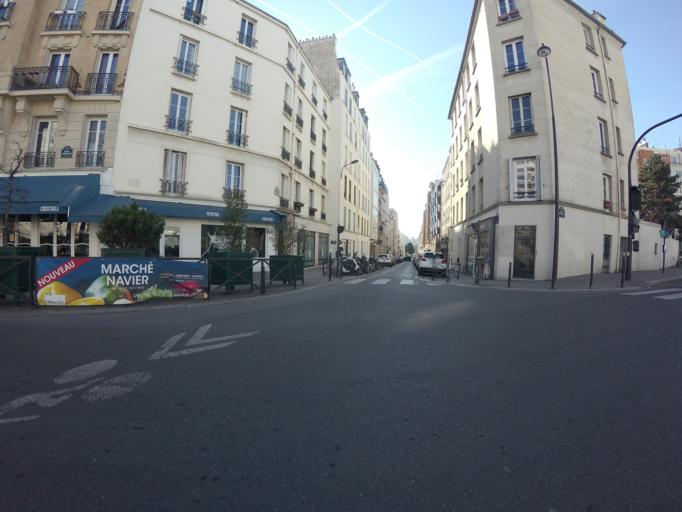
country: FR
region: Ile-de-France
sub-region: Paris
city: Saint-Ouen
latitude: 48.8959
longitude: 2.3229
